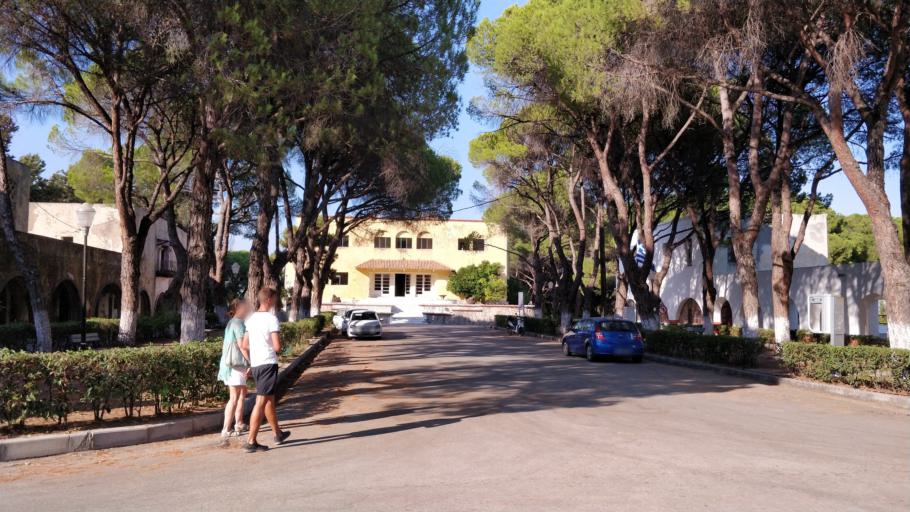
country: GR
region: South Aegean
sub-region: Nomos Dodekanisou
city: Archangelos
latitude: 36.2735
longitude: 28.0267
